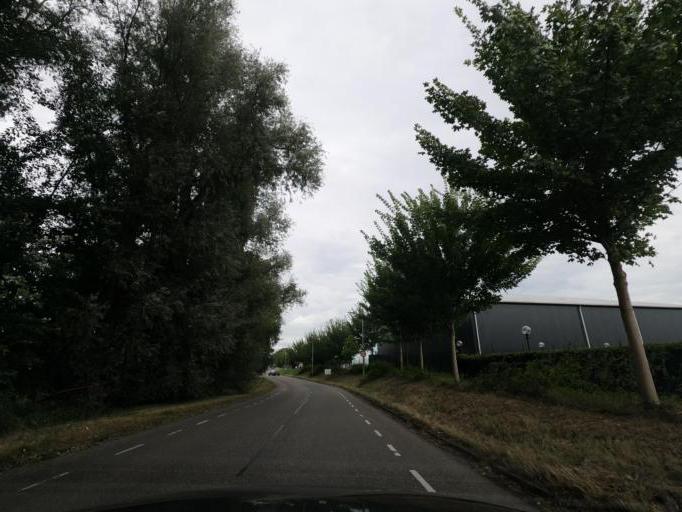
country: NL
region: North Brabant
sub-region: Gemeente Waalwijk
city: Waspik
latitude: 51.6937
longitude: 4.9443
